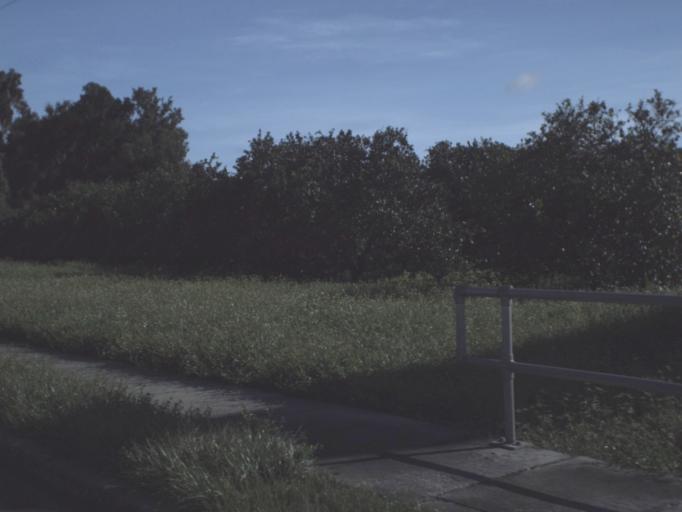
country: US
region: Florida
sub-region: Hardee County
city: Bowling Green
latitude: 27.6490
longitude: -81.8227
